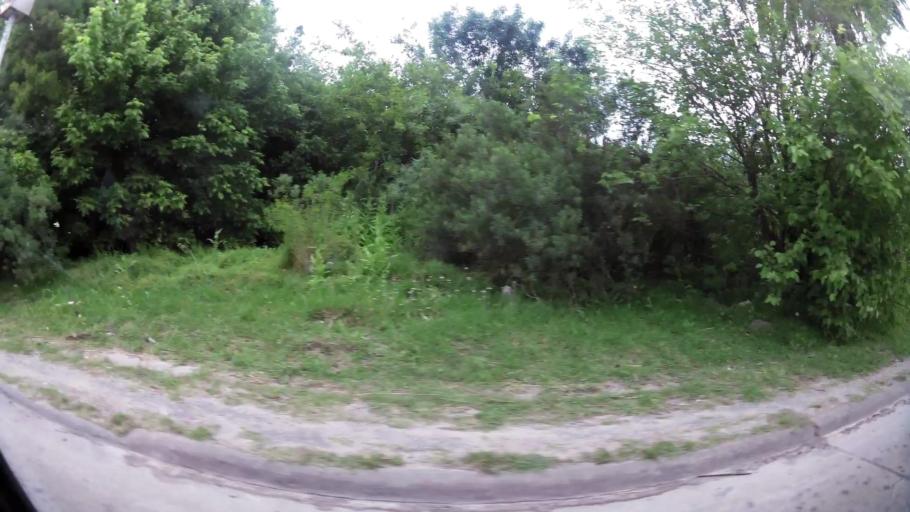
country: AR
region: Buenos Aires
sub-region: Partido de La Plata
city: La Plata
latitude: -34.9734
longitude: -58.0240
